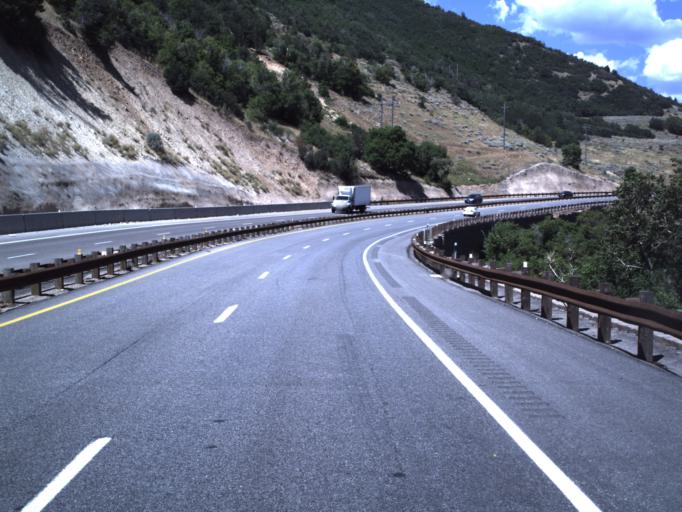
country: US
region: Utah
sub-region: Wasatch County
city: Midway
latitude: 40.3827
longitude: -111.5516
